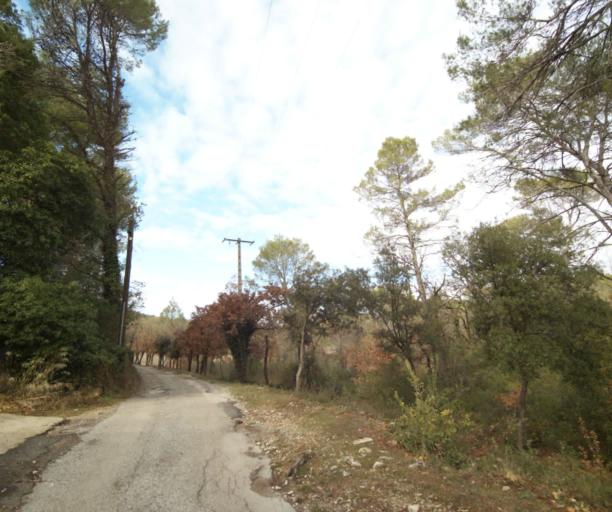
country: FR
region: Provence-Alpes-Cote d'Azur
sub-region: Departement du Var
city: Trans-en-Provence
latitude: 43.5100
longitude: 6.4993
